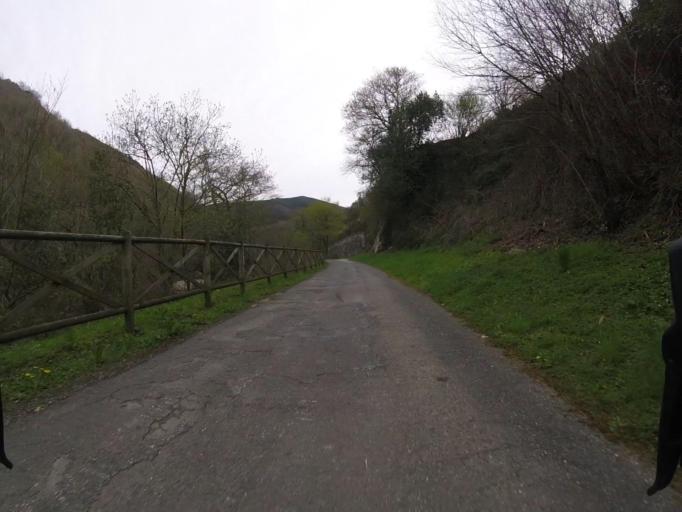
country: ES
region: Navarre
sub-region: Provincia de Navarra
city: Bera
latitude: 43.2986
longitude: -1.7317
